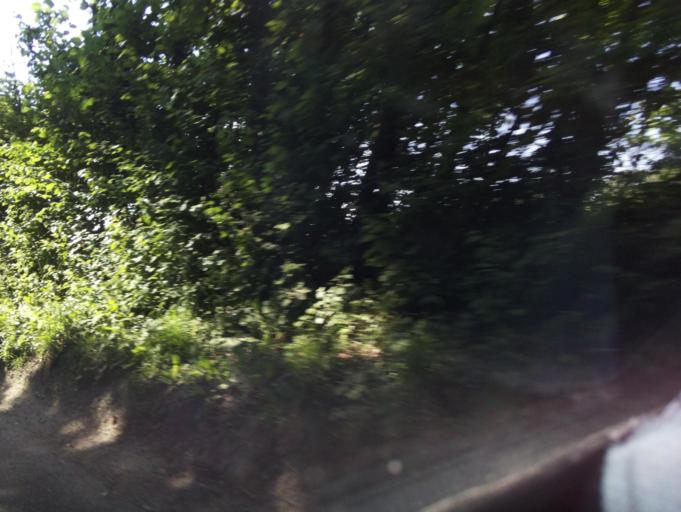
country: GB
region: England
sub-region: Hampshire
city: Andover
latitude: 51.2162
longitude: -1.3928
